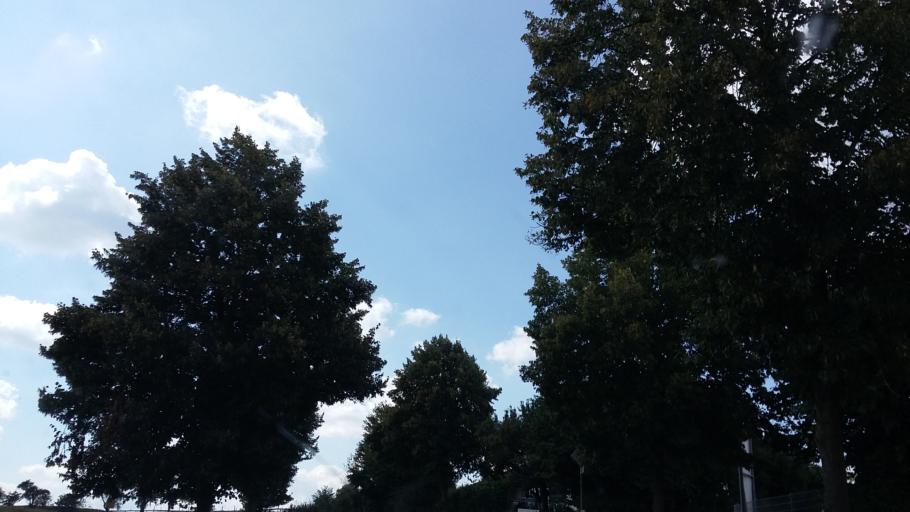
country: DE
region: Bavaria
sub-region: Swabia
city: Pfaffenhofen an der Roth
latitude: 48.3576
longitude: 10.1828
